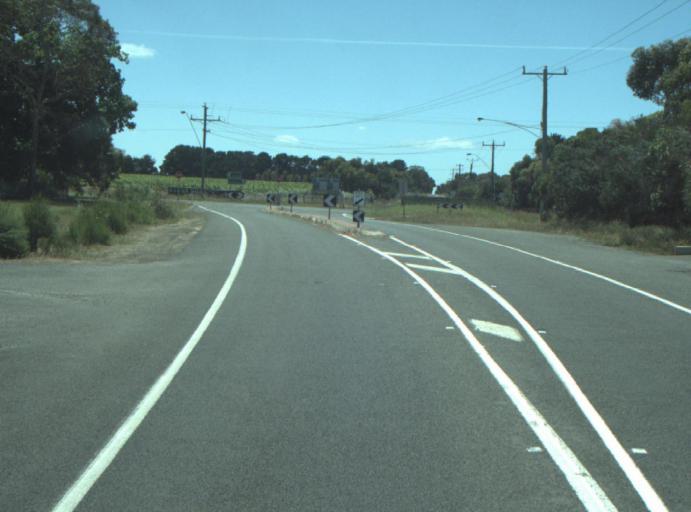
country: AU
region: Victoria
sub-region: Greater Geelong
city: Clifton Springs
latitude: -38.2427
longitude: 144.5721
